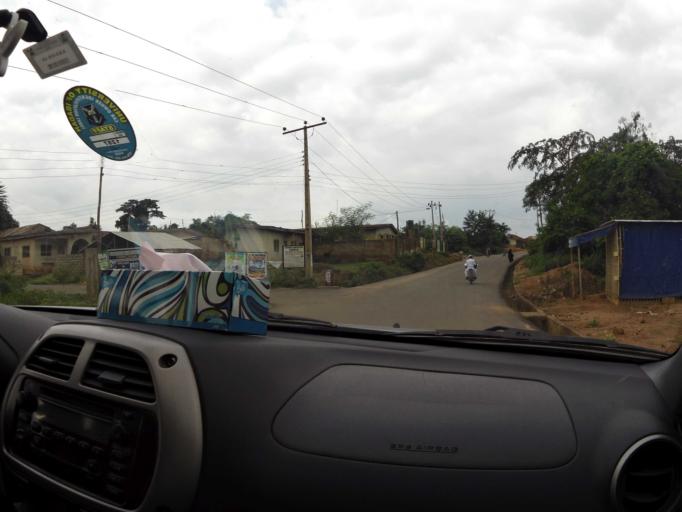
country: NG
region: Oyo
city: Moniya
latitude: 7.5256
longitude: 3.9247
